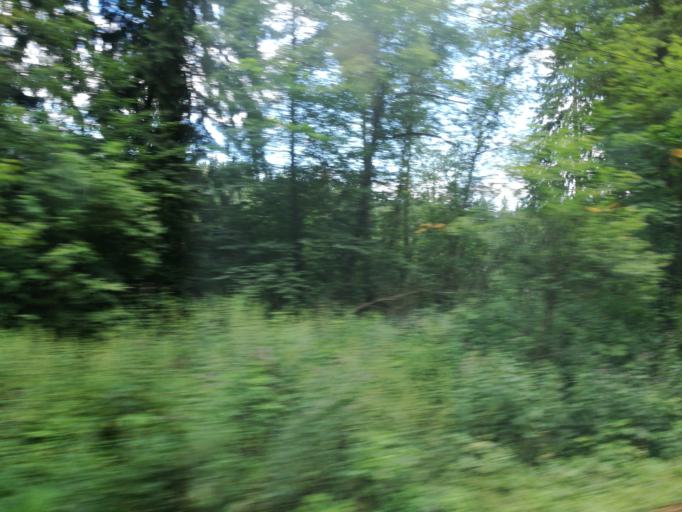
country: RO
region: Brasov
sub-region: Oras Predeal
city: Predeal
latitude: 45.5382
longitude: 25.5872
